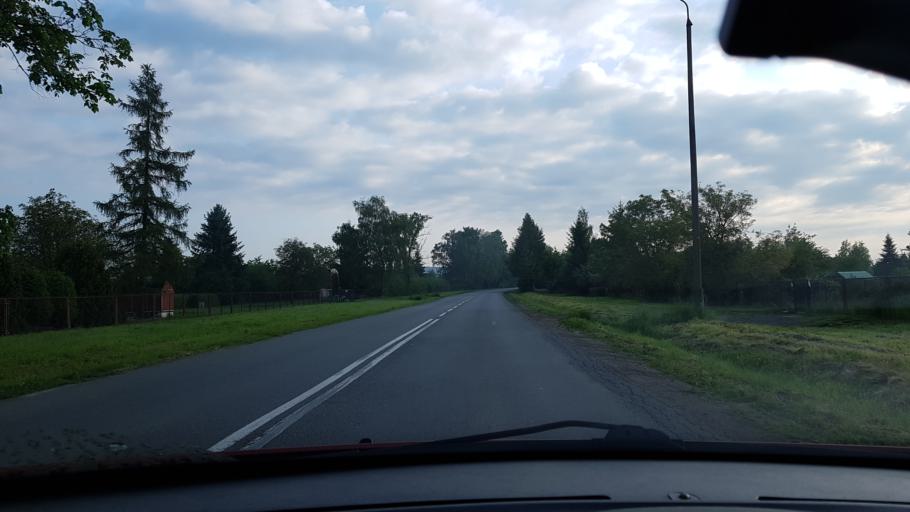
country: PL
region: Lower Silesian Voivodeship
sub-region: Powiat zabkowicki
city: Zabkowice Slaskie
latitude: 50.6032
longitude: 16.8204
